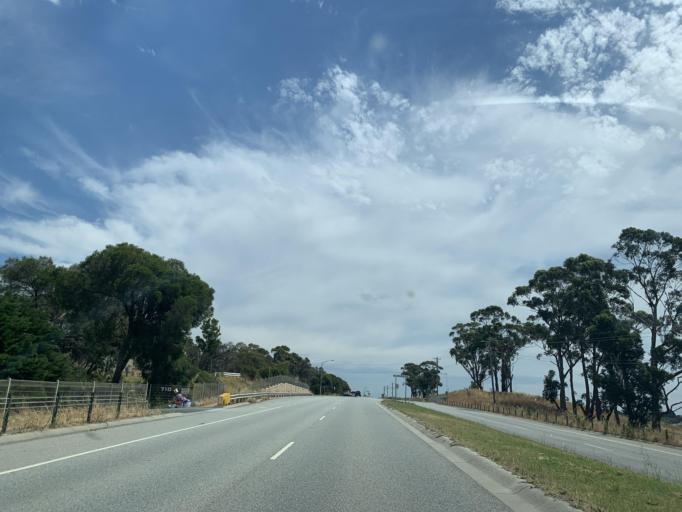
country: AU
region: Victoria
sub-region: Casey
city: Cranbourne South
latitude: -38.1283
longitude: 145.2407
